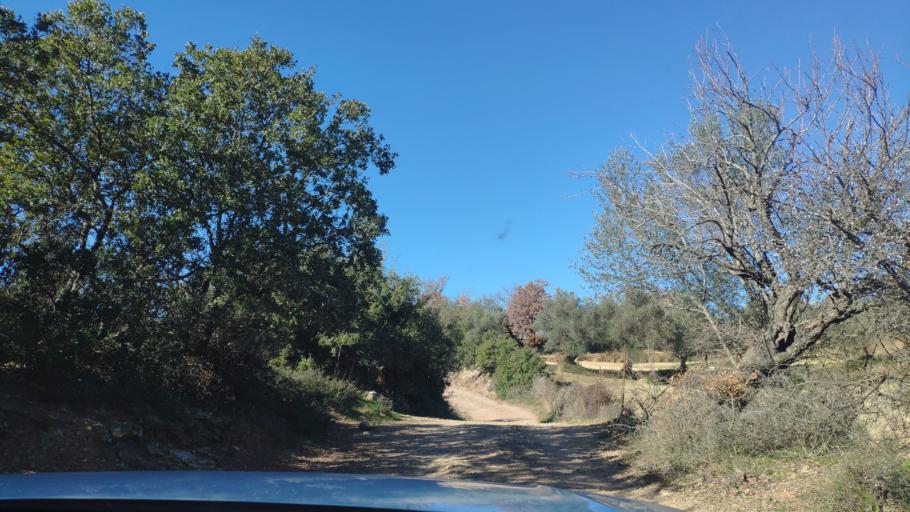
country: GR
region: West Greece
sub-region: Nomos Aitolias kai Akarnanias
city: Thermo
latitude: 38.5807
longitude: 21.6318
